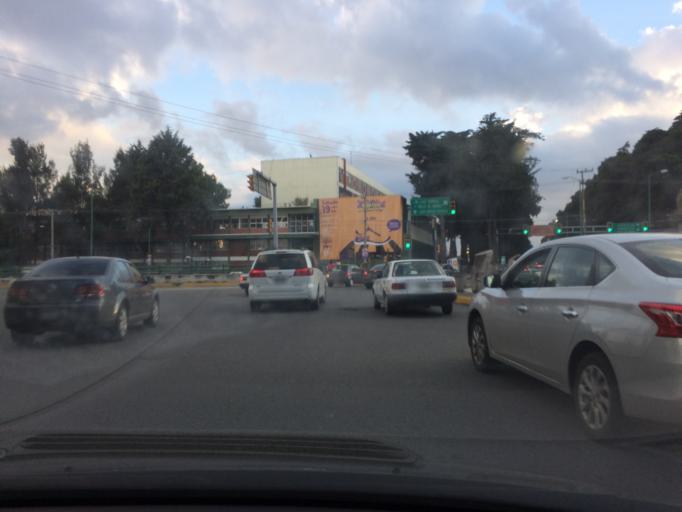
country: MX
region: Mexico
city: San Buenaventura
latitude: 19.2736
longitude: -99.6598
